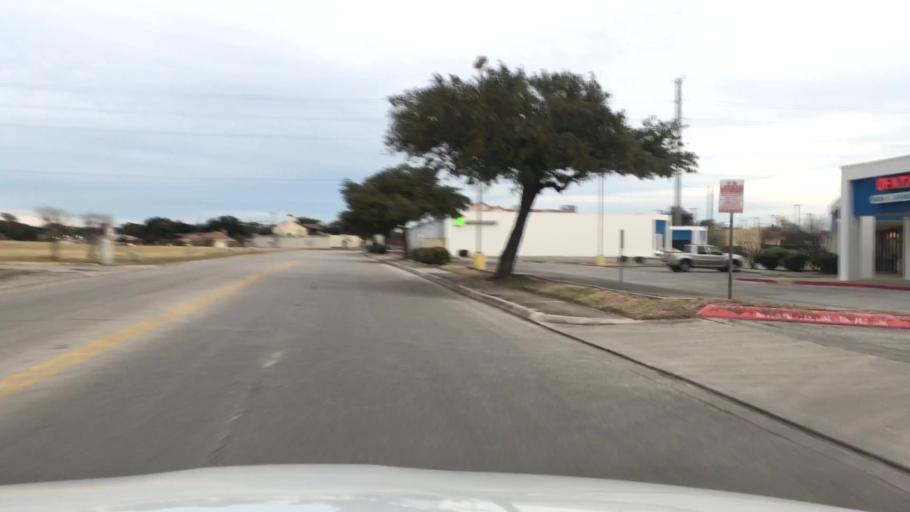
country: US
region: Texas
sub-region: Bexar County
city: Windcrest
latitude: 29.5118
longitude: -98.3930
